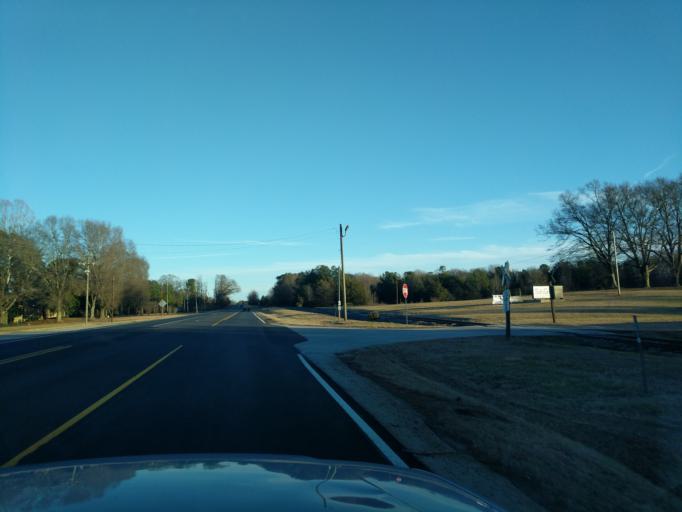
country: US
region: Georgia
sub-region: Franklin County
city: Gumlog
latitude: 34.5107
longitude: -83.2185
